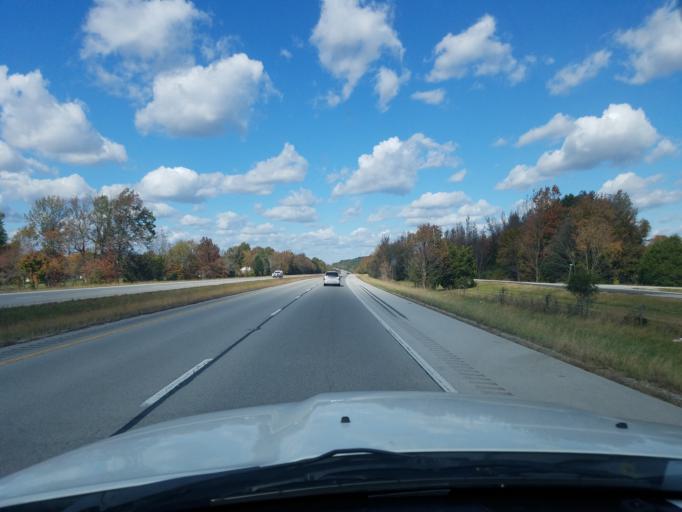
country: US
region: Kentucky
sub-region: Butler County
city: Morgantown
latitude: 37.0780
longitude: -86.6155
